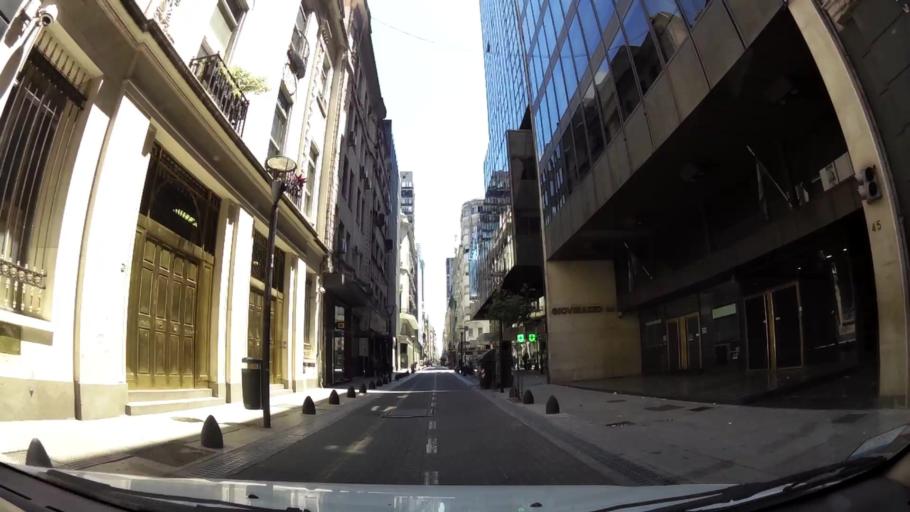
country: AR
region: Buenos Aires F.D.
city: Buenos Aires
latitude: -34.6044
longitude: -58.3731
